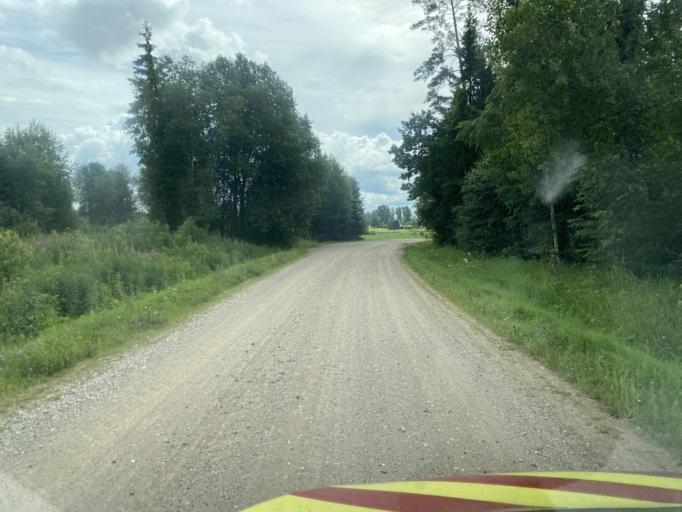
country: EE
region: Viljandimaa
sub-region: Karksi vald
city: Karksi-Nuia
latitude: 58.0600
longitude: 25.5393
